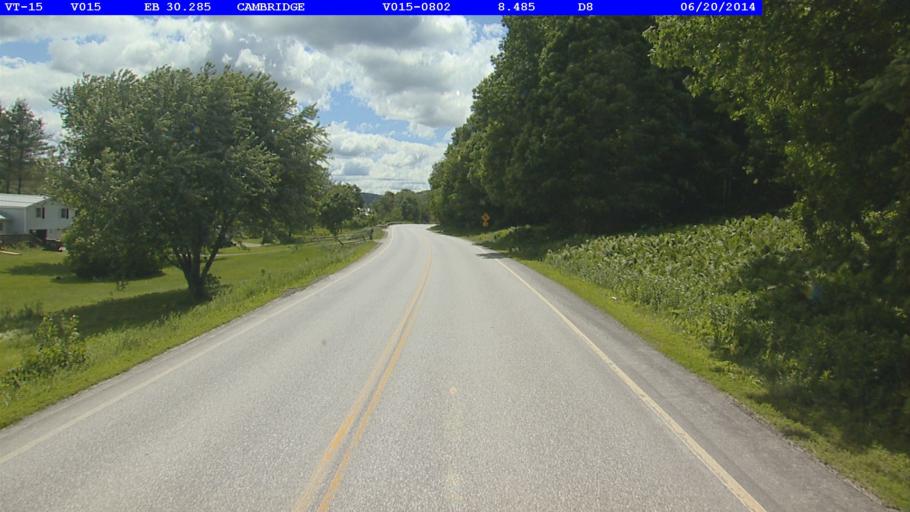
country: US
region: Vermont
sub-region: Lamoille County
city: Johnson
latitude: 44.6626
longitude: -72.7738
